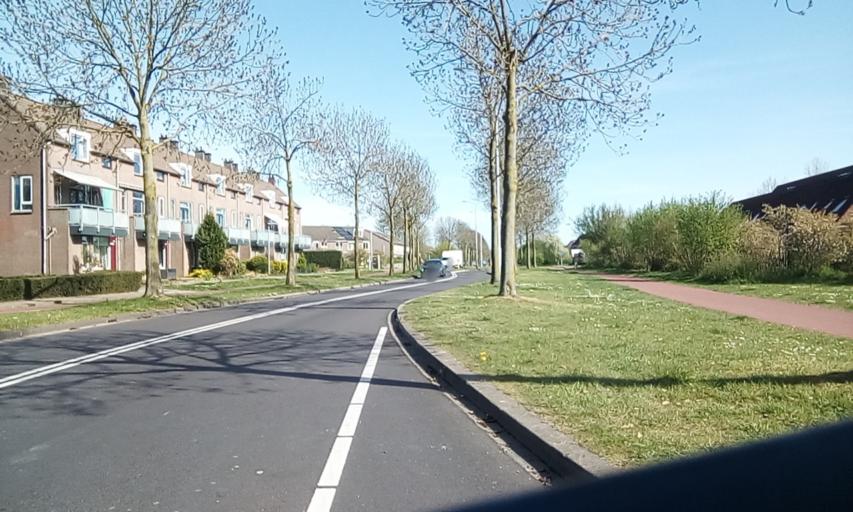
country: NL
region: Gelderland
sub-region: Gemeente Wijchen
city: Wijchen
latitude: 51.7990
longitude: 5.7250
